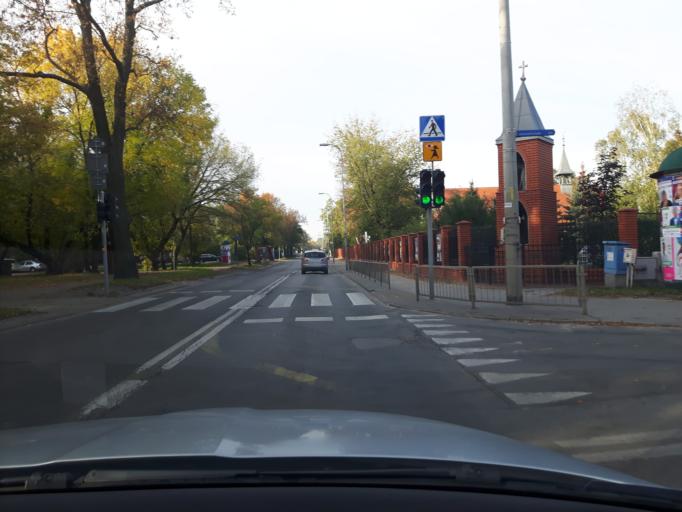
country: PL
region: Masovian Voivodeship
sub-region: Warszawa
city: Praga Poludnie
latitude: 52.2666
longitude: 21.0703
